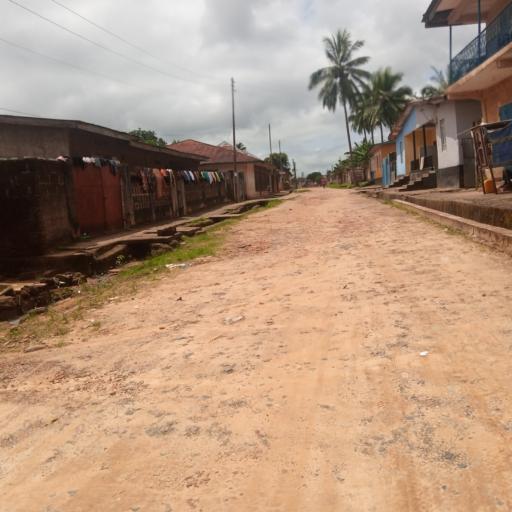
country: SL
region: Eastern Province
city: Kenema
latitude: 7.8901
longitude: -11.1864
